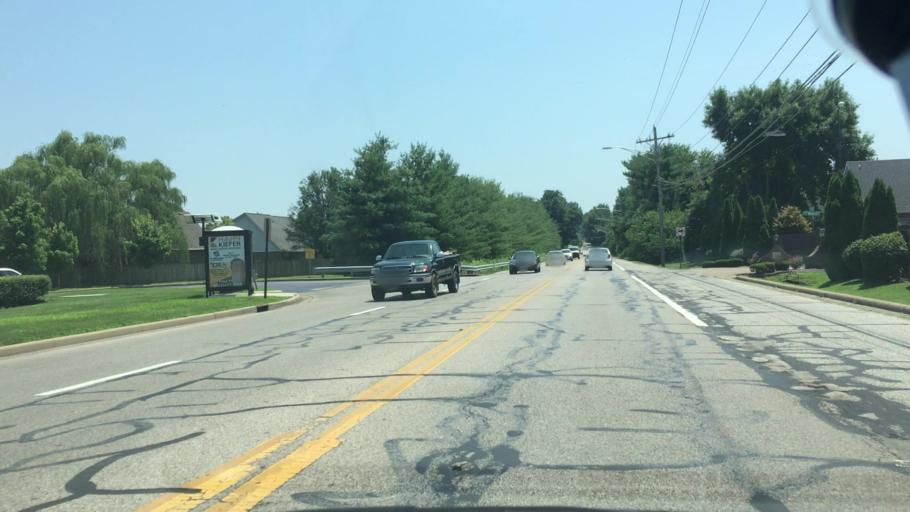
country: US
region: Indiana
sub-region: Vanderburgh County
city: Melody Hill
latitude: 37.9735
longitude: -87.4743
